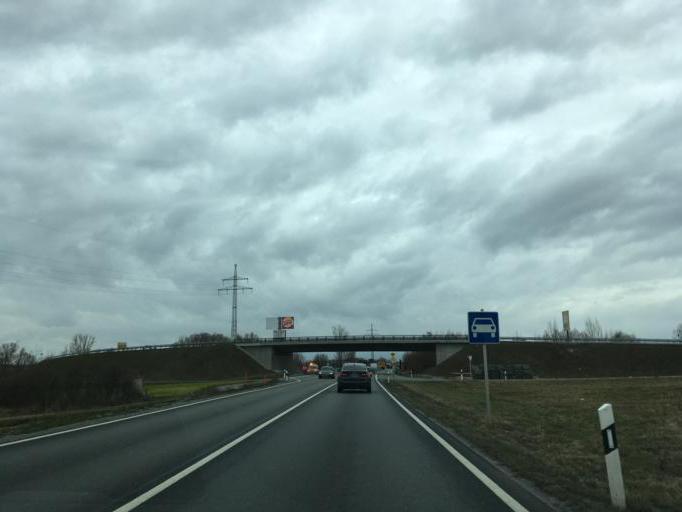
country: DE
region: Bavaria
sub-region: Lower Bavaria
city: Landau an der Isar
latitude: 48.6876
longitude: 12.6754
